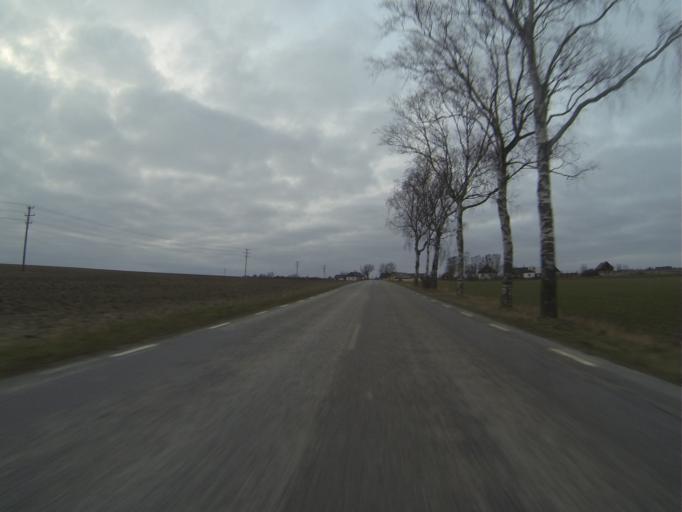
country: SE
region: Skane
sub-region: Lunds Kommun
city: Genarp
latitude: 55.6309
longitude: 13.3773
